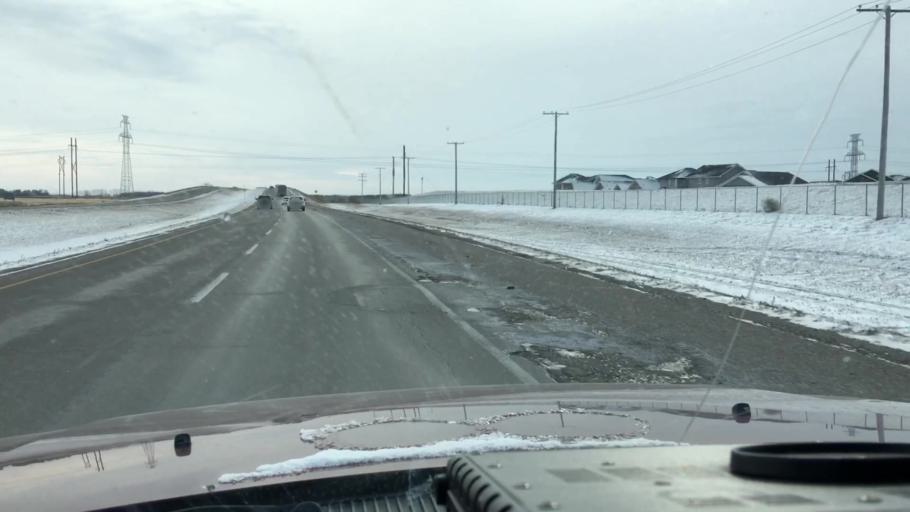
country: CA
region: Saskatchewan
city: Saskatoon
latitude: 52.0749
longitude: -106.6048
